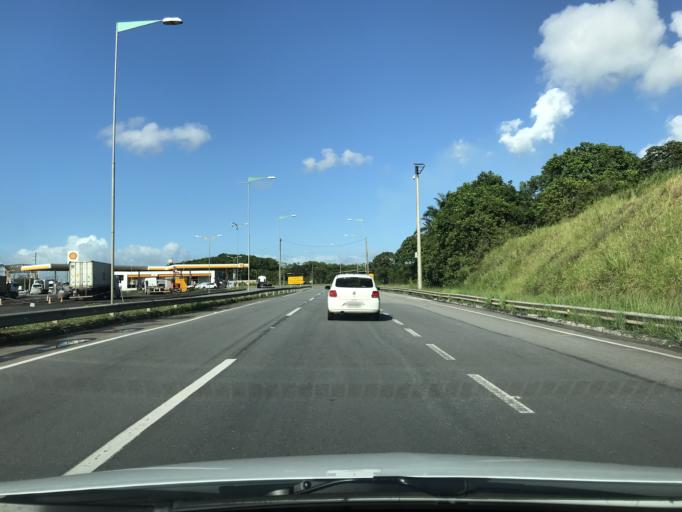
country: BR
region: Pernambuco
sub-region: Ipojuca
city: Ipojuca
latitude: -8.3662
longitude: -35.0080
